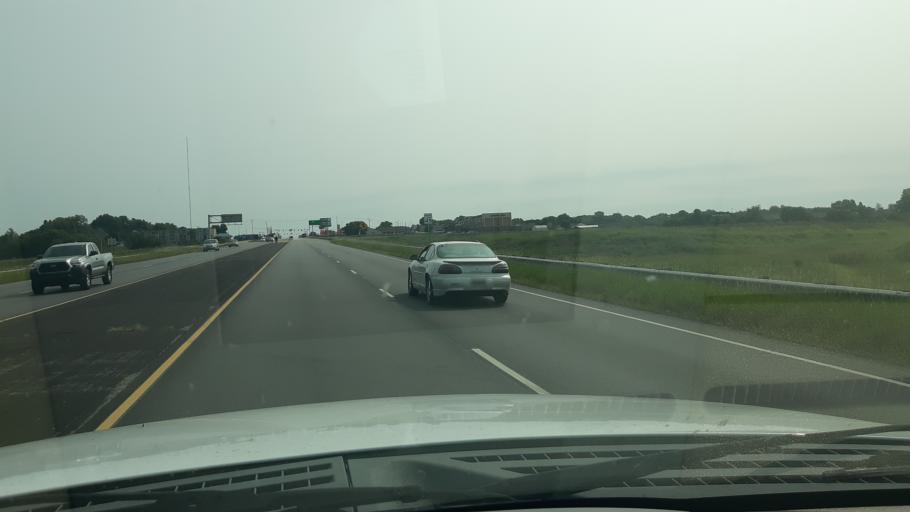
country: US
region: Indiana
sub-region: Gibson County
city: Princeton
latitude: 38.3554
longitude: -87.6018
